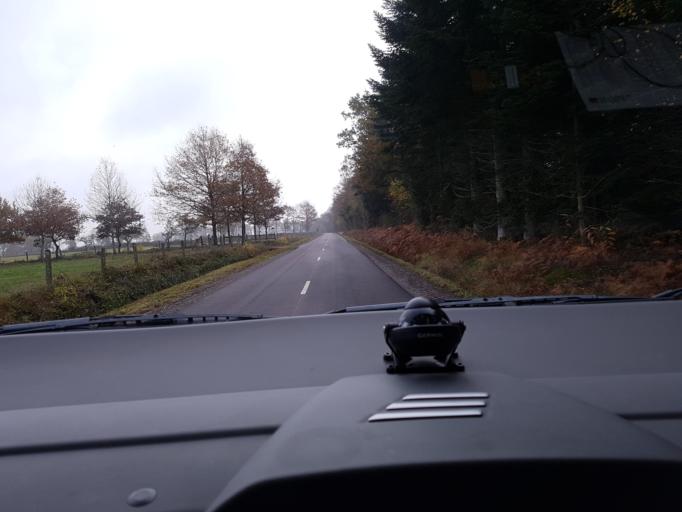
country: FR
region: Lower Normandy
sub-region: Departement de l'Orne
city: Mortree
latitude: 48.6348
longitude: 0.0169
